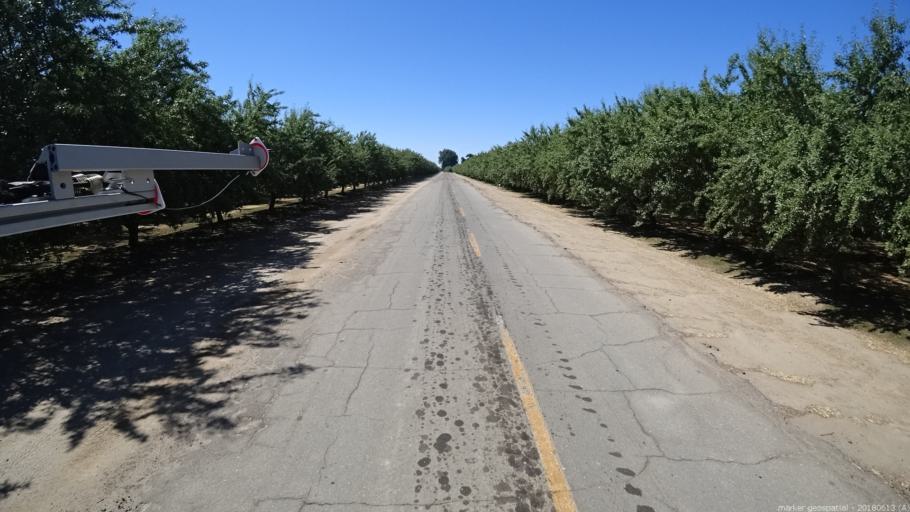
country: US
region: California
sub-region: Madera County
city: Chowchilla
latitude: 37.0207
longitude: -120.3648
